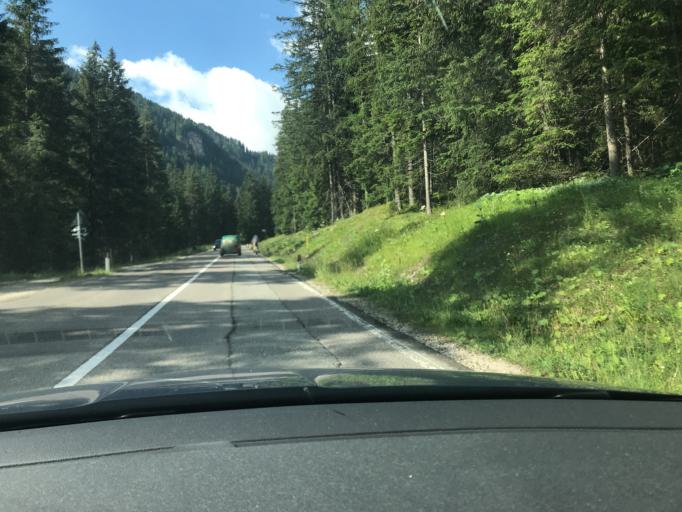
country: IT
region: Trentino-Alto Adige
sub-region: Bolzano
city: Corvara in Badia
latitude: 46.5660
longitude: 11.8873
